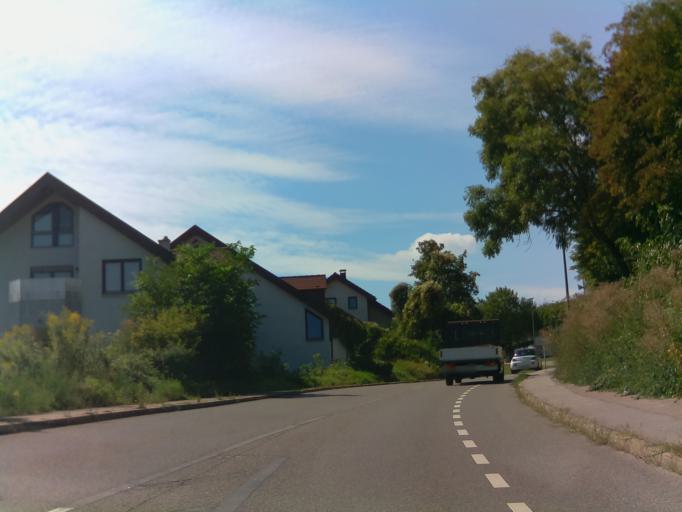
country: DE
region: Baden-Wuerttemberg
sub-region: Regierungsbezirk Stuttgart
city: Leonberg
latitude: 48.8016
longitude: 9.0058
